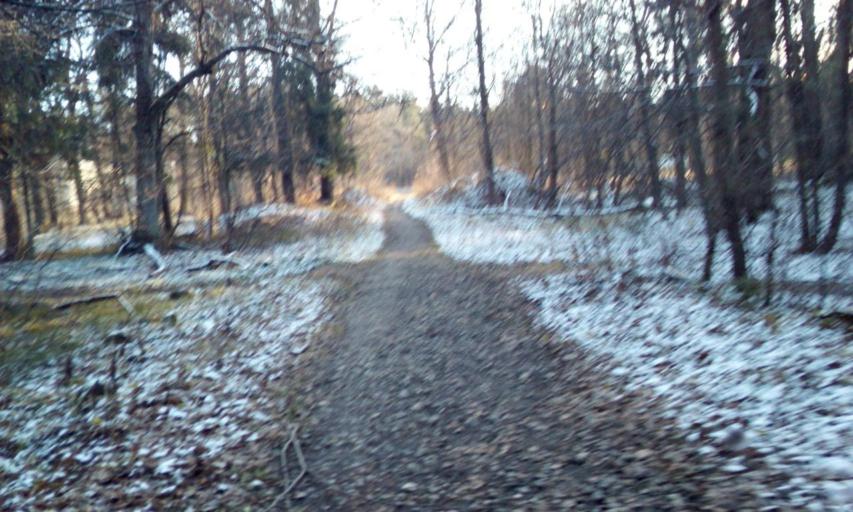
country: RU
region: Moskovskaya
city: Aprelevka
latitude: 55.5443
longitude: 37.0966
